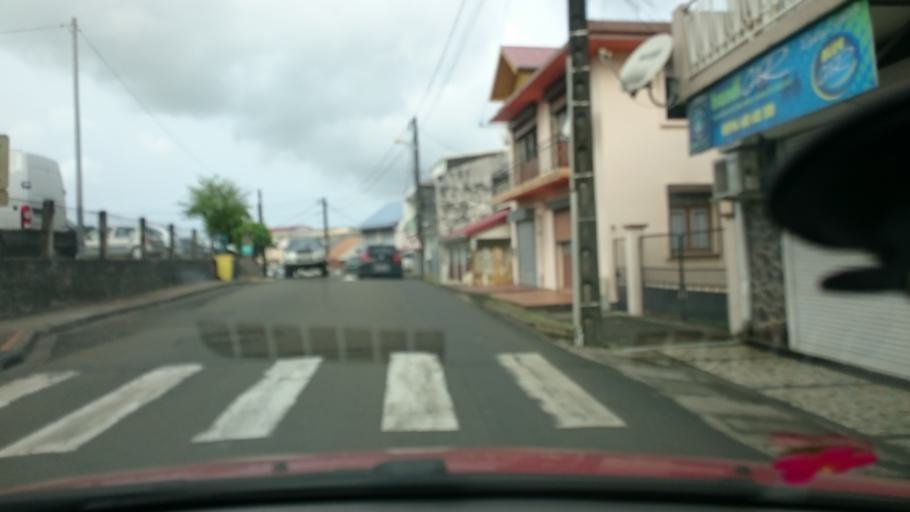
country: MQ
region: Martinique
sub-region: Martinique
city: Saint-Esprit
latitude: 14.5629
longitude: -60.9370
